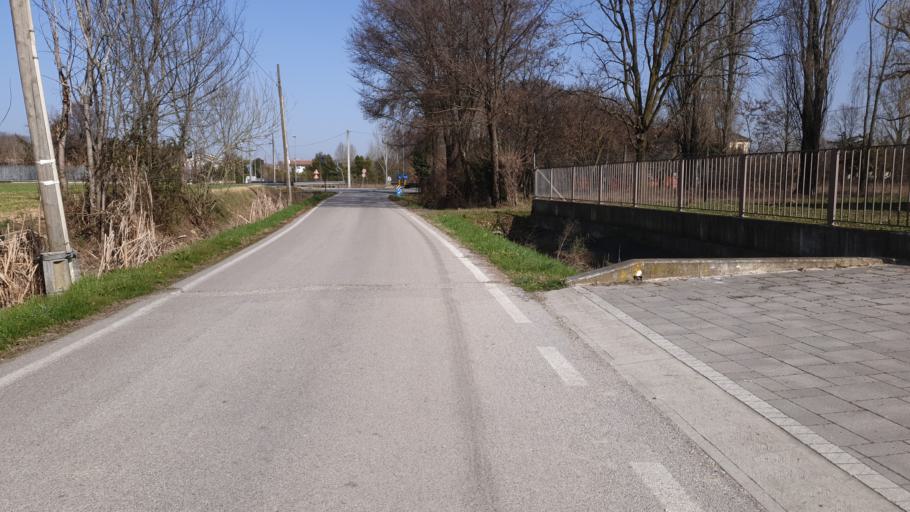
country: IT
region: Veneto
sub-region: Provincia di Padova
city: Camposampiero
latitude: 45.5511
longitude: 11.9220
